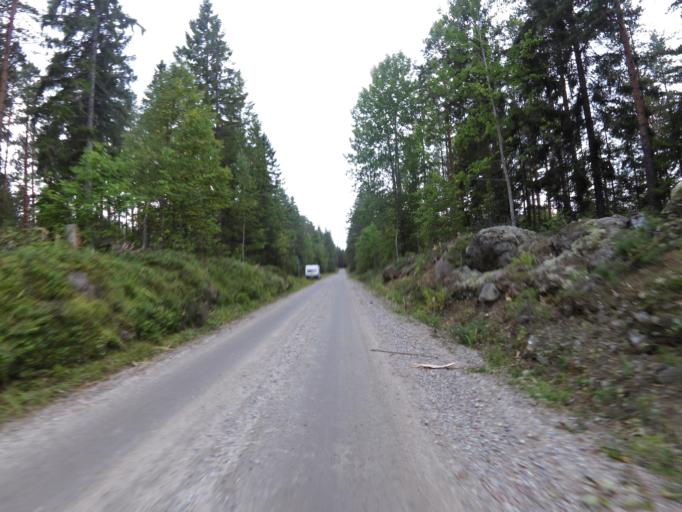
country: SE
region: Gaevleborg
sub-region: Sandvikens Kommun
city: Sandviken
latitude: 60.7557
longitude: 16.8545
